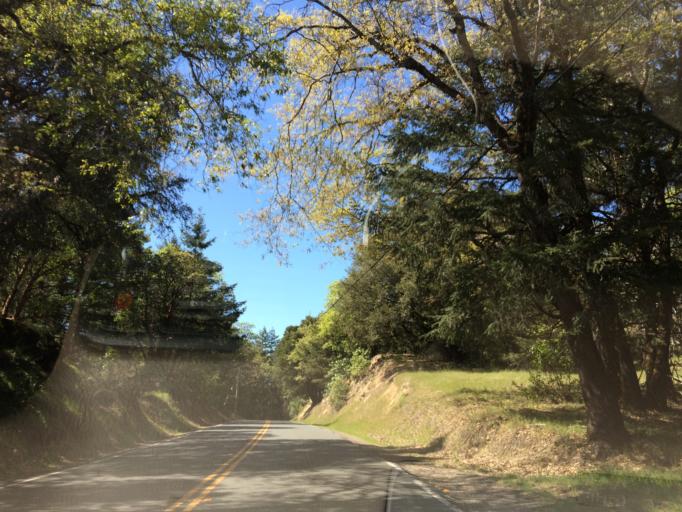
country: US
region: California
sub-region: Santa Clara County
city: Saratoga
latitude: 37.2337
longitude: -122.1008
